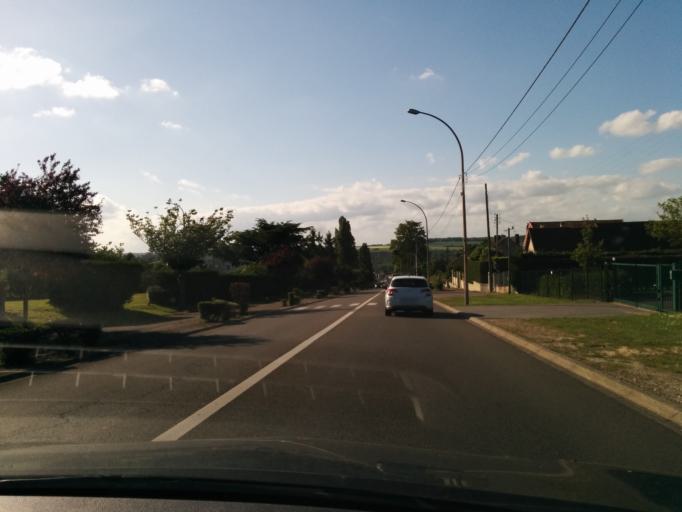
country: FR
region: Ile-de-France
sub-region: Departement des Yvelines
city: Freneuse
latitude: 49.0346
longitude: 1.6005
